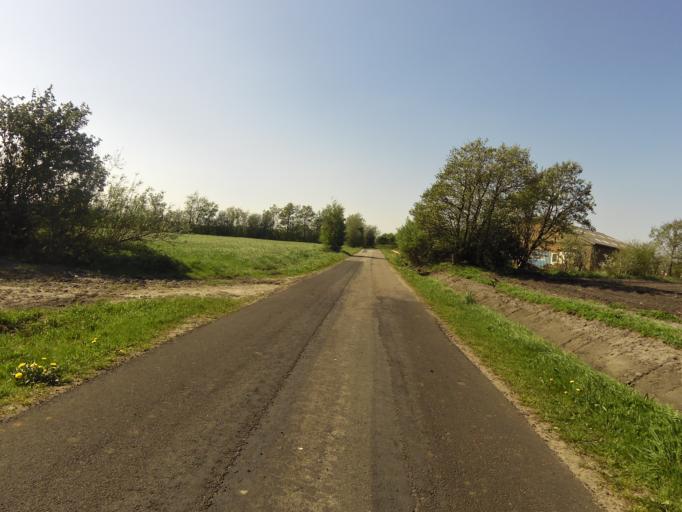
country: DK
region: South Denmark
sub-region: Tonder Kommune
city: Sherrebek
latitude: 55.2125
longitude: 8.8420
